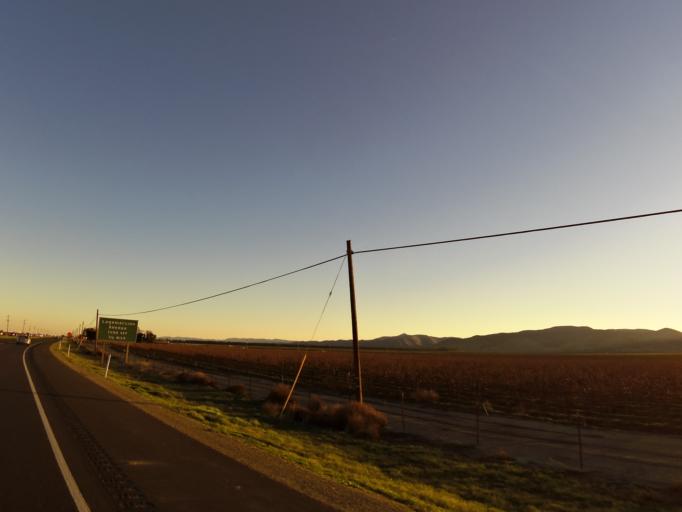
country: US
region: California
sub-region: Monterey County
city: Greenfield
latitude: 36.2924
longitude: -121.1993
